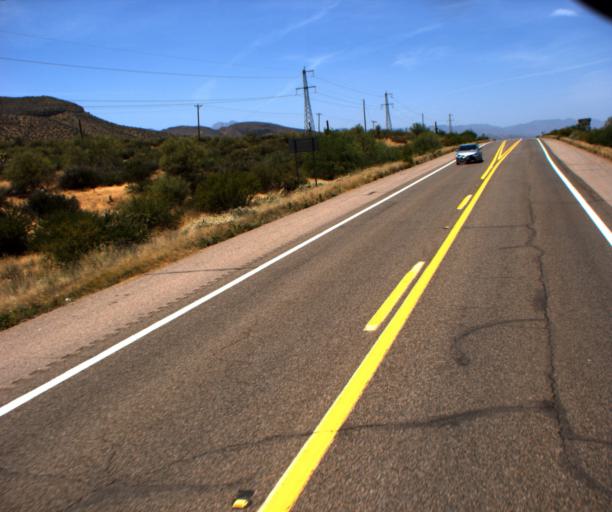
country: US
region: Arizona
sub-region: Gila County
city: Tonto Basin
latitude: 33.6528
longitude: -111.1031
